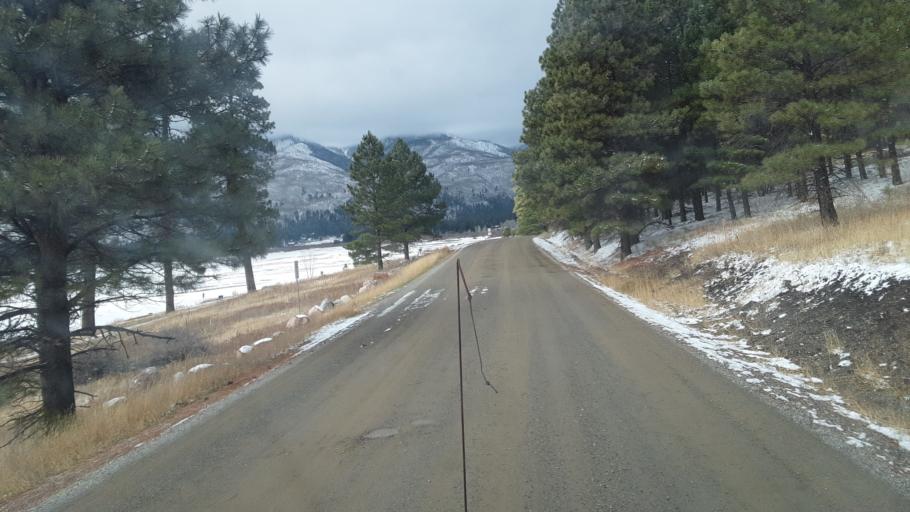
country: US
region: Colorado
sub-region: La Plata County
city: Bayfield
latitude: 37.4266
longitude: -107.5382
